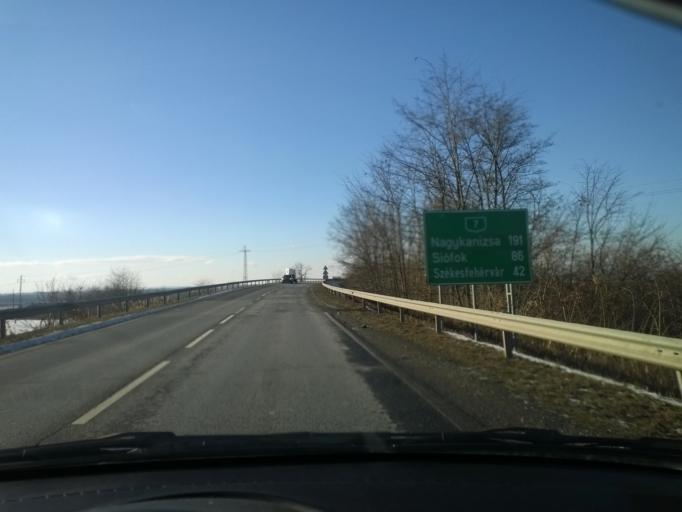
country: HU
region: Pest
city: Erd
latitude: 47.3607
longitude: 18.9033
